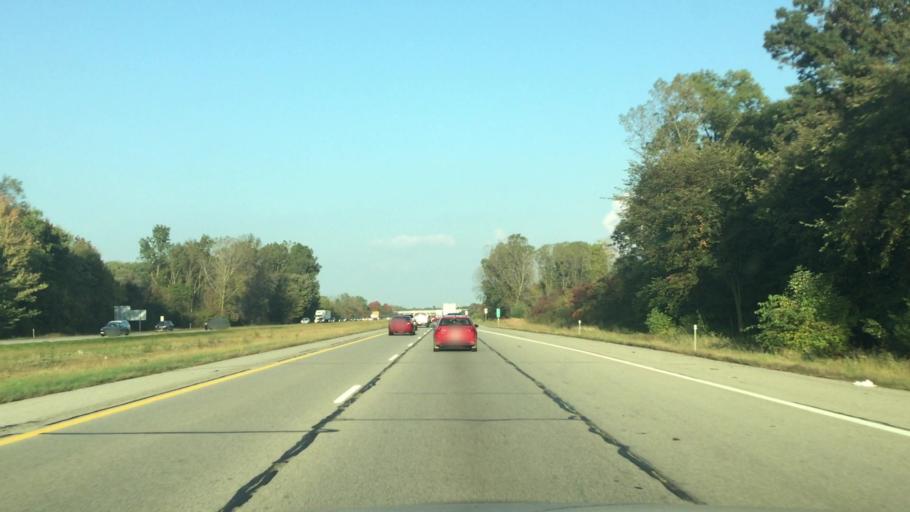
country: US
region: Michigan
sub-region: Wayne County
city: Plymouth
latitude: 42.3636
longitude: -83.5611
